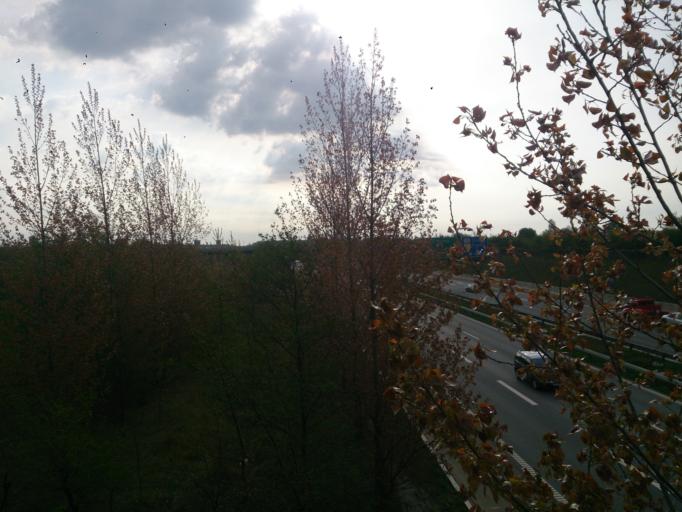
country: DK
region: Capital Region
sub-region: Tarnby Kommune
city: Tarnby
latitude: 55.6281
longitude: 12.5813
